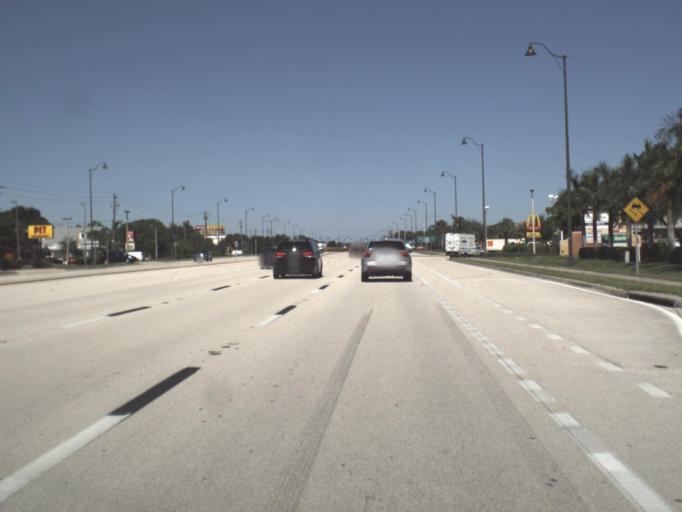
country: US
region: Florida
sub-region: Lee County
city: Bonita Springs
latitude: 26.3258
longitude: -81.8054
